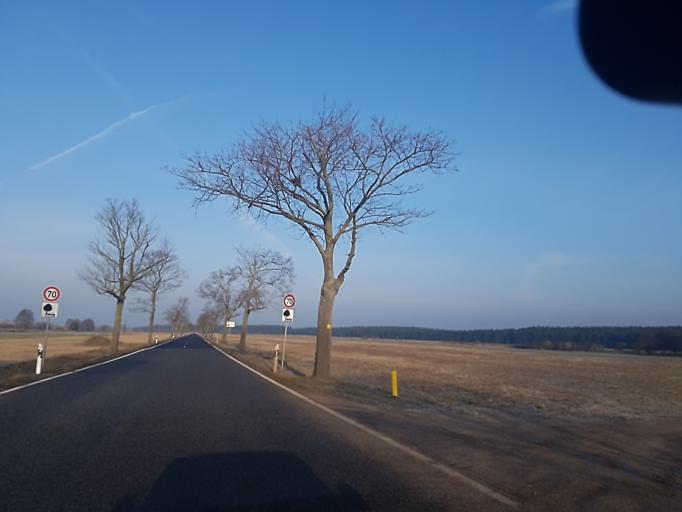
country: DE
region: Brandenburg
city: Golzow
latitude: 52.2625
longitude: 12.6598
